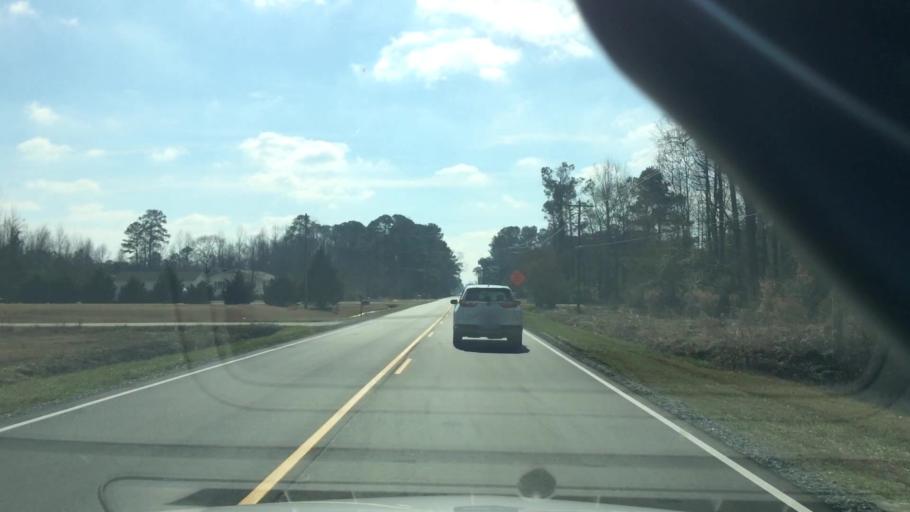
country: US
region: North Carolina
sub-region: Duplin County
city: Beulaville
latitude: 34.9665
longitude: -77.7633
